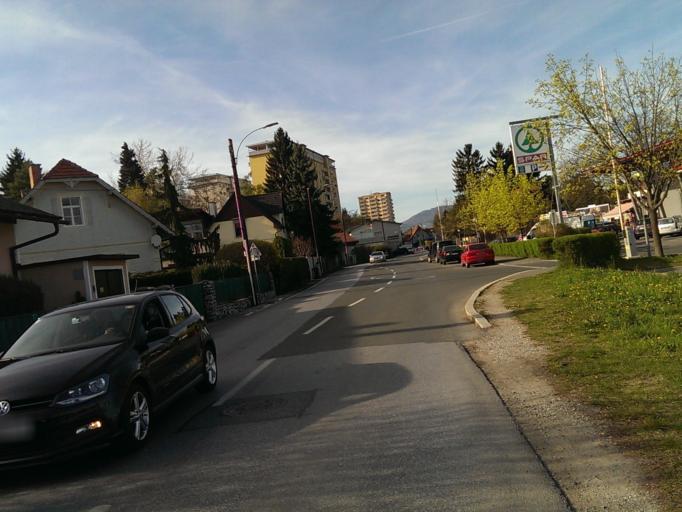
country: AT
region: Styria
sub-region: Graz Stadt
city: Graz
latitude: 47.0430
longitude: 15.4496
